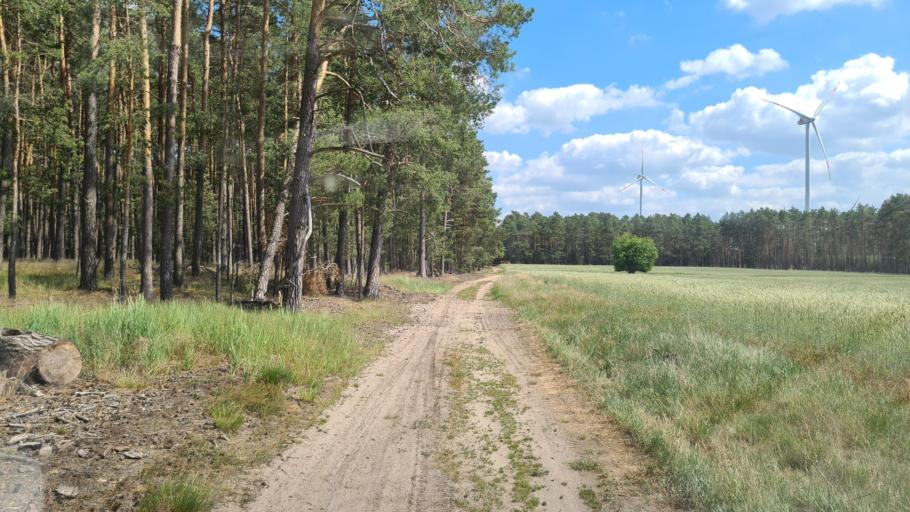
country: DE
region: Brandenburg
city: Sallgast
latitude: 51.6528
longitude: 13.8173
